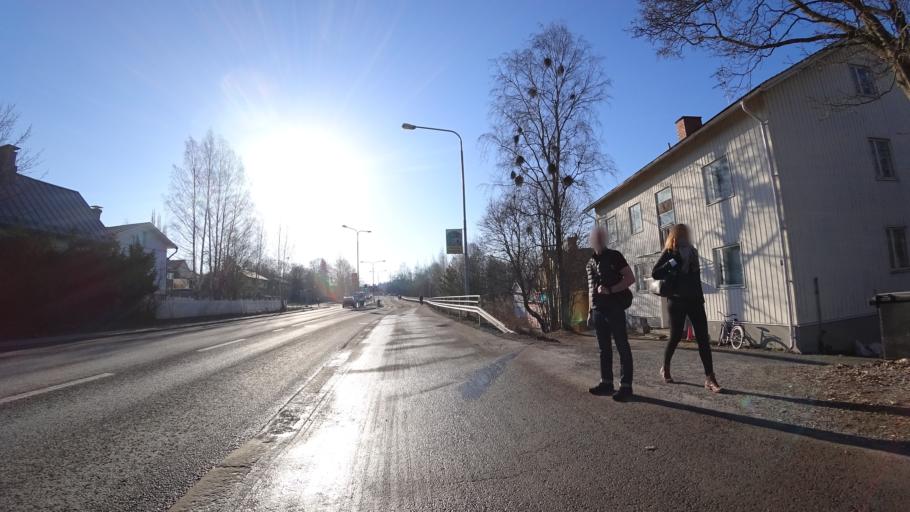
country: FI
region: Pirkanmaa
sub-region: Tampere
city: Pirkkala
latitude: 61.5071
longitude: 23.6938
